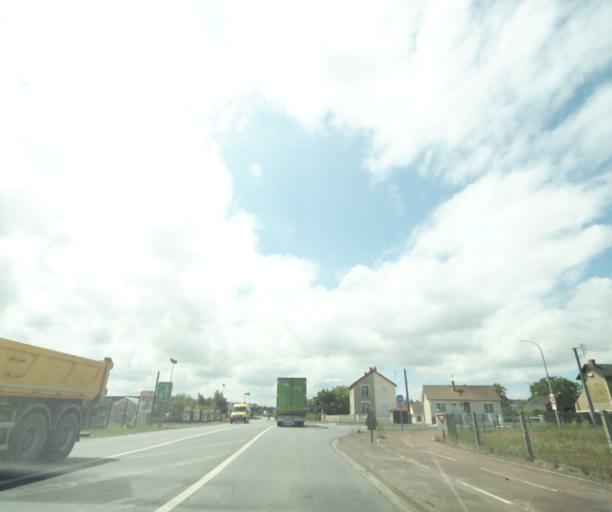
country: FR
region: Poitou-Charentes
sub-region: Departement des Deux-Sevres
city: Thouars
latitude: 46.9835
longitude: -0.1989
